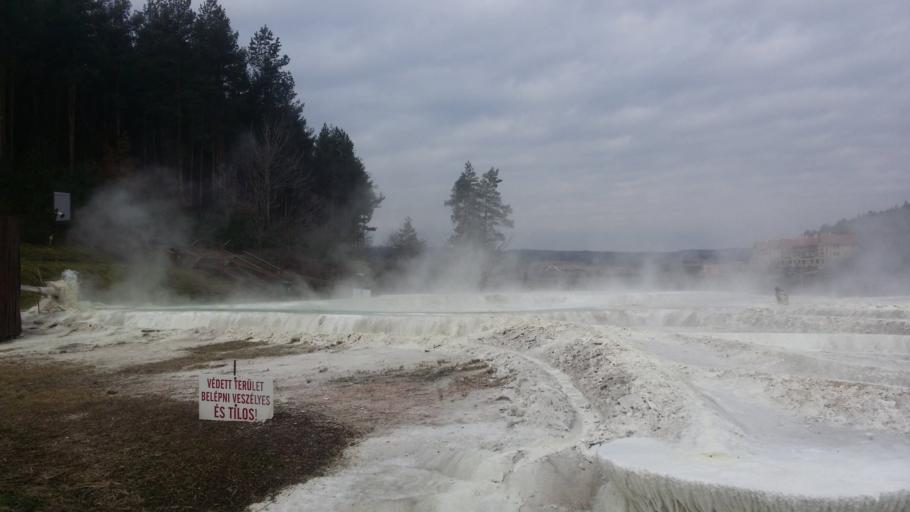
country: HU
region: Heves
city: Egerszalok
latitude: 47.8530
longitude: 20.3347
